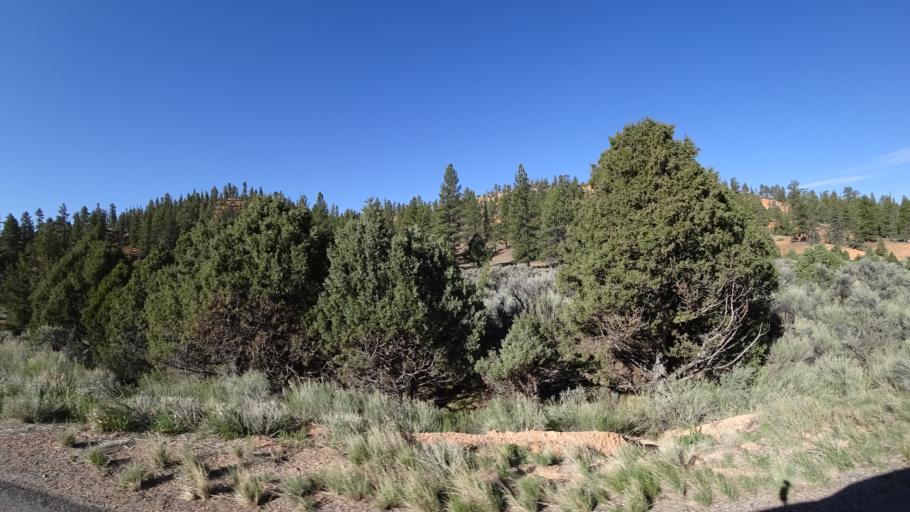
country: US
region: Utah
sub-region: Garfield County
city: Panguitch
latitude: 37.7333
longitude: -112.2827
